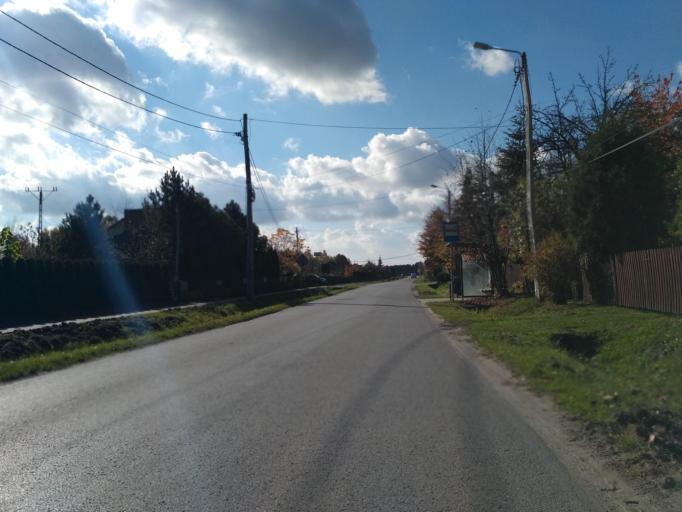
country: PL
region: Subcarpathian Voivodeship
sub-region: Powiat rzeszowski
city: Glogow Malopolski
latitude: 50.1480
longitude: 21.9535
